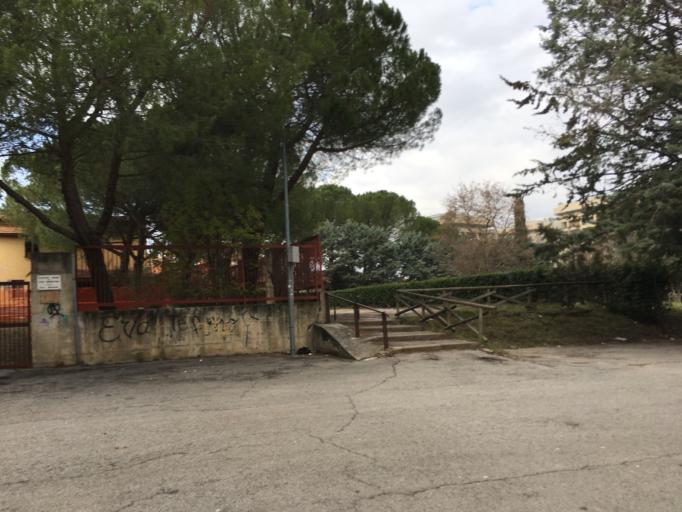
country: IT
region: Umbria
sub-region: Provincia di Perugia
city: Perugia
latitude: 43.1027
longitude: 12.3719
